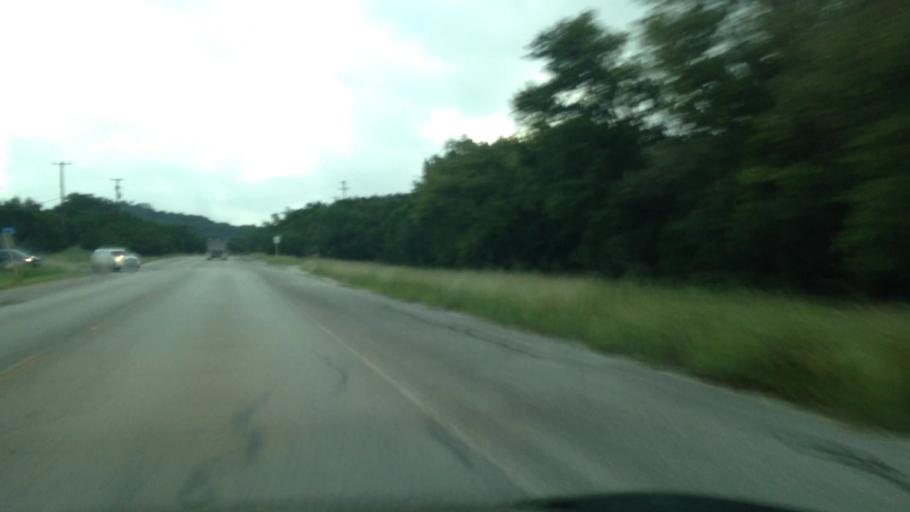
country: US
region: Texas
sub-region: Bexar County
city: Cross Mountain
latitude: 29.6291
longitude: -98.6041
